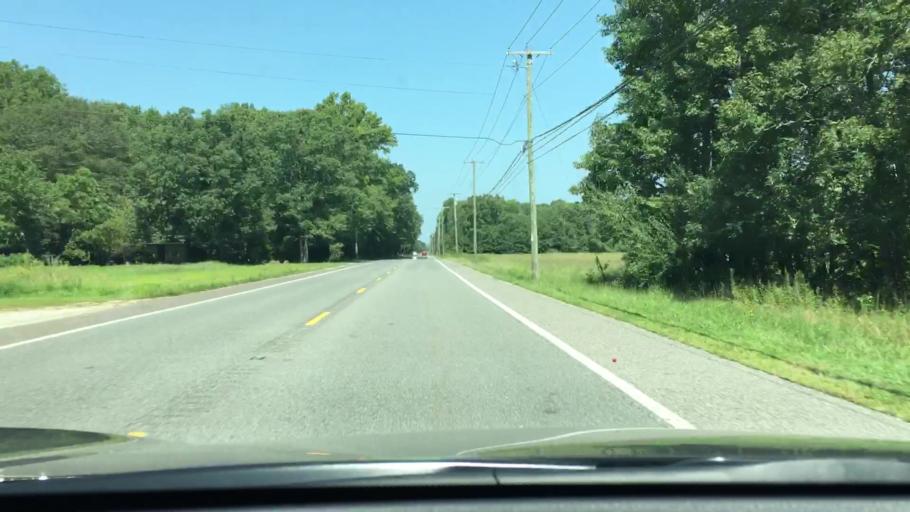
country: US
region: New Jersey
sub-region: Cumberland County
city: Laurel Lake
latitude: 39.3074
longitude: -75.0058
